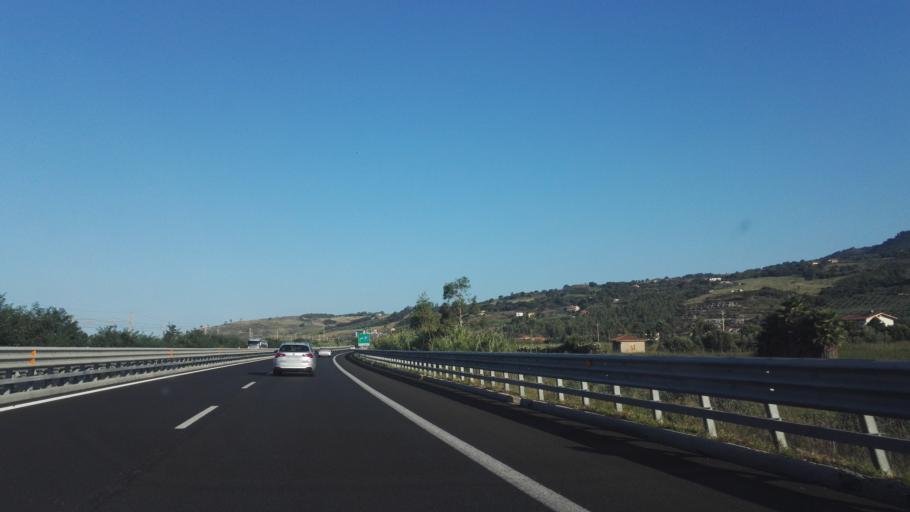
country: IT
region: Calabria
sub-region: Provincia di Catanzaro
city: Gizzeria
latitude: 38.9435
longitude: 16.1923
